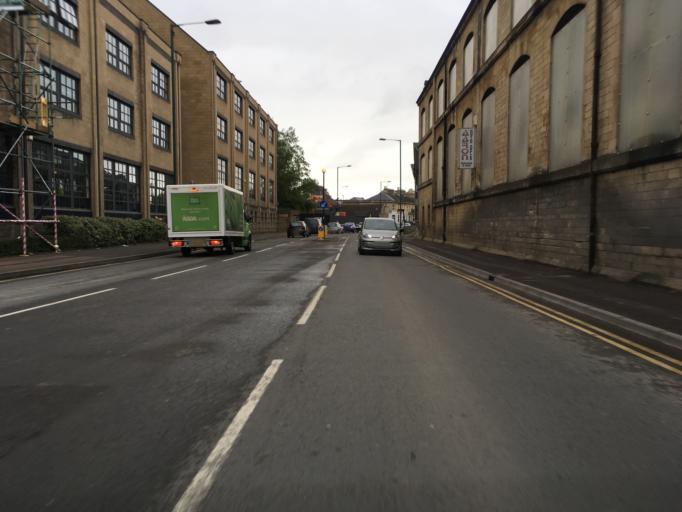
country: GB
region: England
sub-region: Bath and North East Somerset
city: Bath
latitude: 51.3786
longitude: -2.3665
